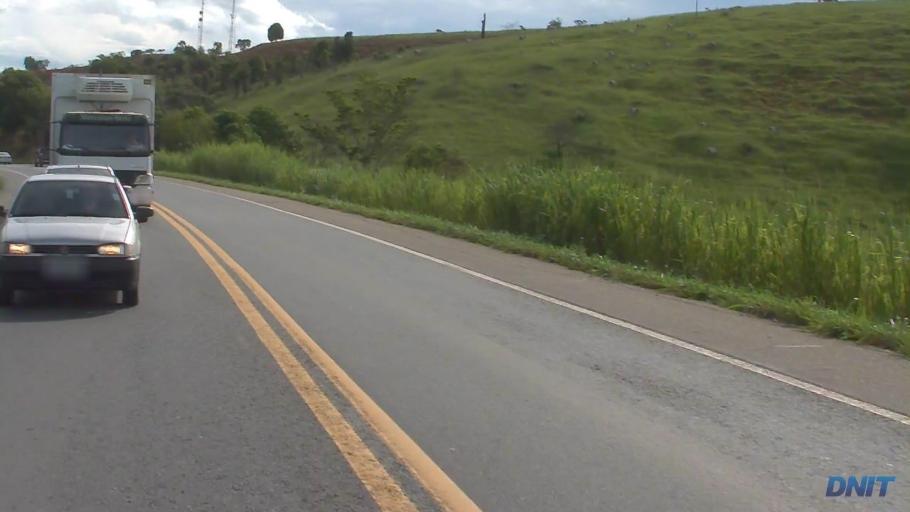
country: BR
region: Minas Gerais
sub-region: Belo Oriente
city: Belo Oriente
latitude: -19.2187
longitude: -42.3086
